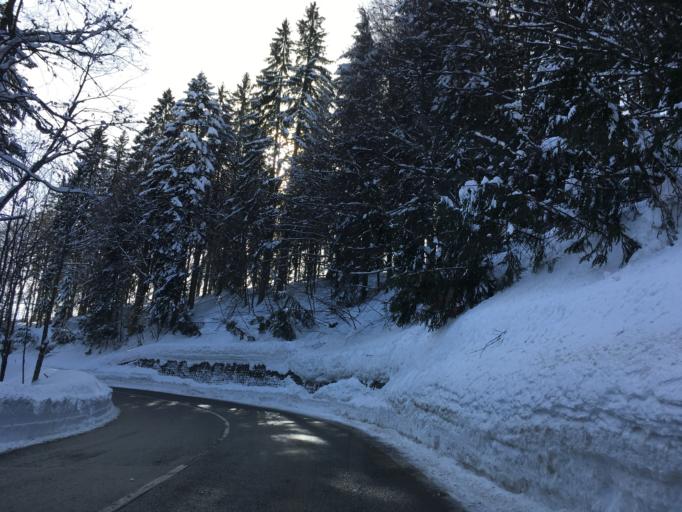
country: DE
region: Bavaria
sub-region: Upper Bavaria
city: Bayrischzell
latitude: 47.6800
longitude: 12.0342
